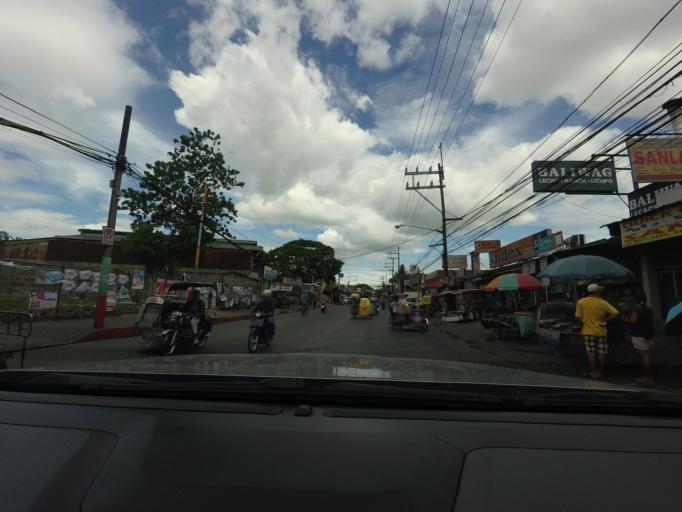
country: PH
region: Calabarzon
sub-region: Province of Rizal
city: Pateros
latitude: 14.5571
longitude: 121.0857
